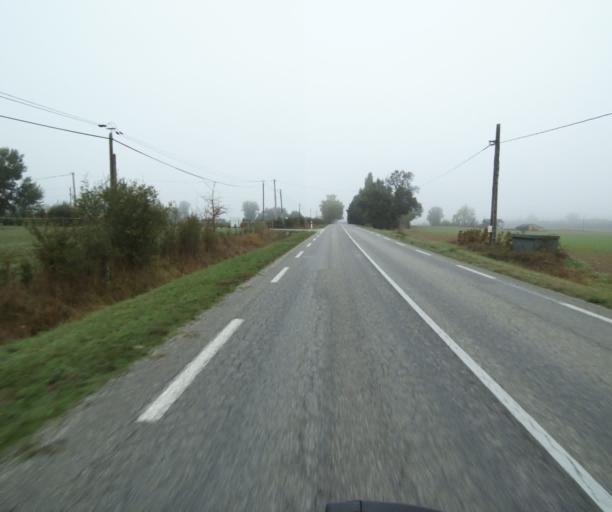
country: FR
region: Midi-Pyrenees
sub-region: Departement du Tarn-et-Garonne
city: Saint-Nauphary
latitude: 43.9494
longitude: 1.4510
